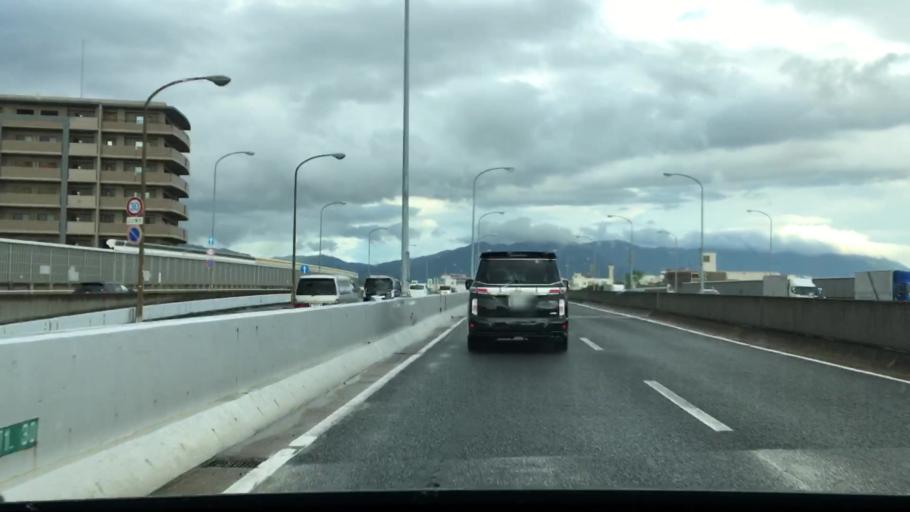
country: JP
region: Fukuoka
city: Fukuoka-shi
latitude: 33.6343
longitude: 130.4256
